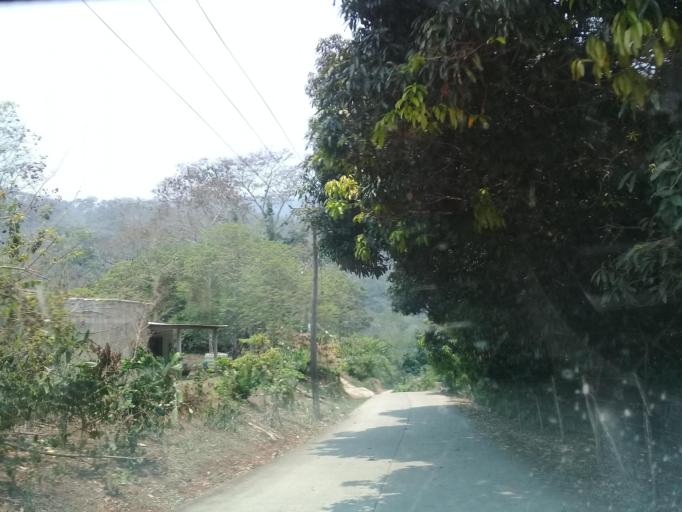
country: MX
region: Veracruz
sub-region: Tezonapa
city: Laguna Chica (Pueblo Nuevo)
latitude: 18.5700
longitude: -96.7282
